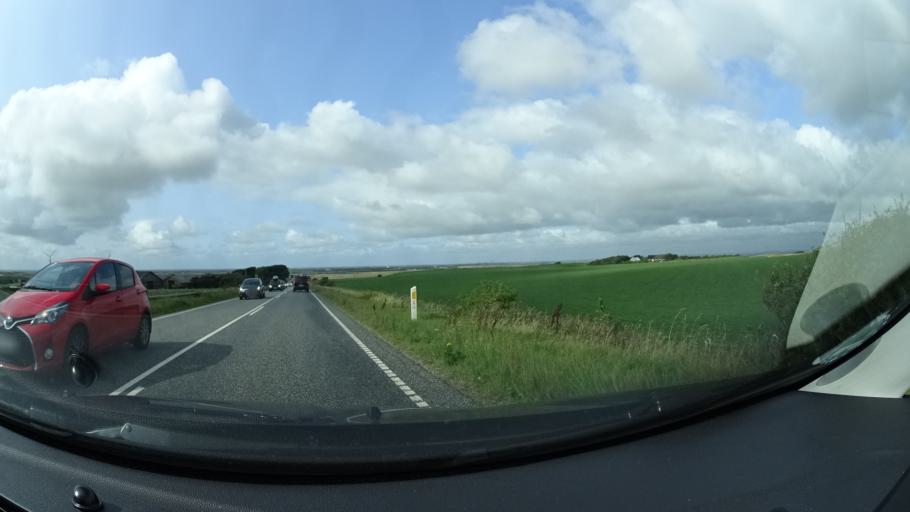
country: DK
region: Central Jutland
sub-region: Lemvig Kommune
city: Harboore
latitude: 56.5847
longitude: 8.1972
